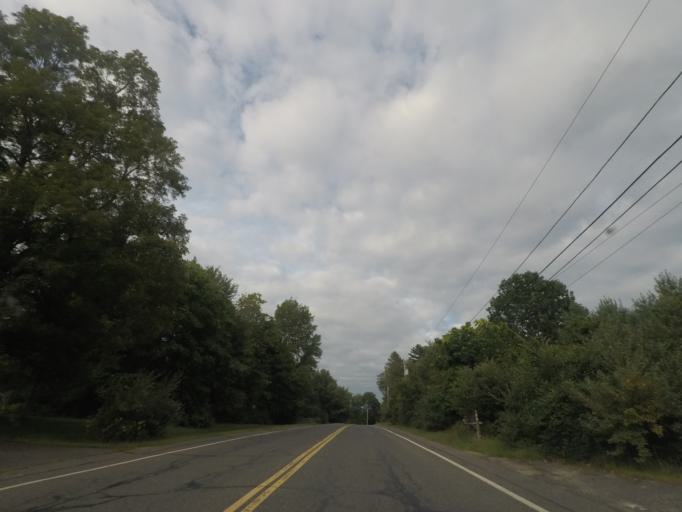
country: US
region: Massachusetts
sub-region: Hampden County
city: Palmer
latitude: 42.1898
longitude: -72.2917
